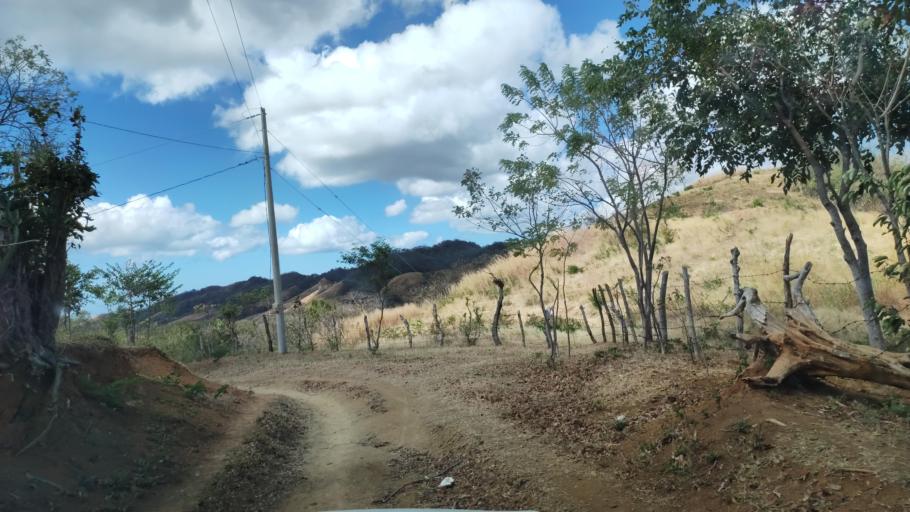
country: NI
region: Carazo
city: Santa Teresa
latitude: 11.6445
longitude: -86.2158
